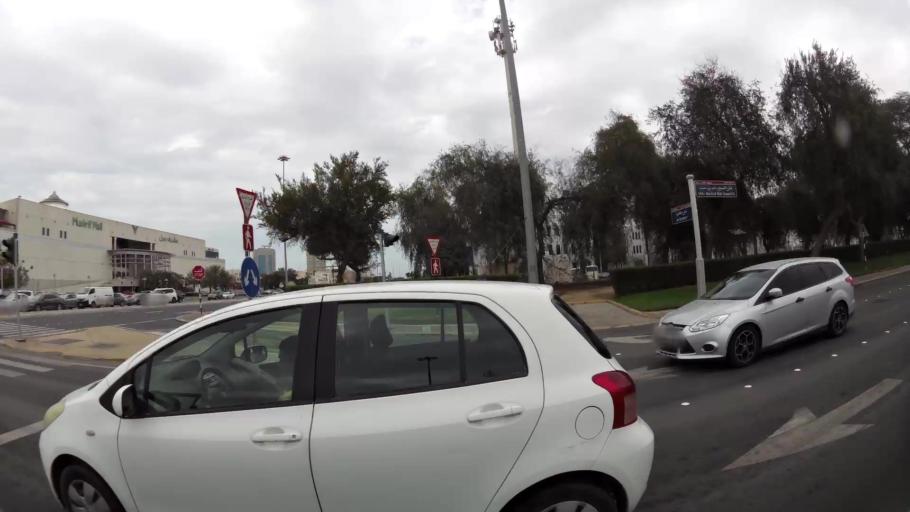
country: AE
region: Abu Dhabi
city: Abu Dhabi
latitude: 24.4326
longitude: 54.4141
